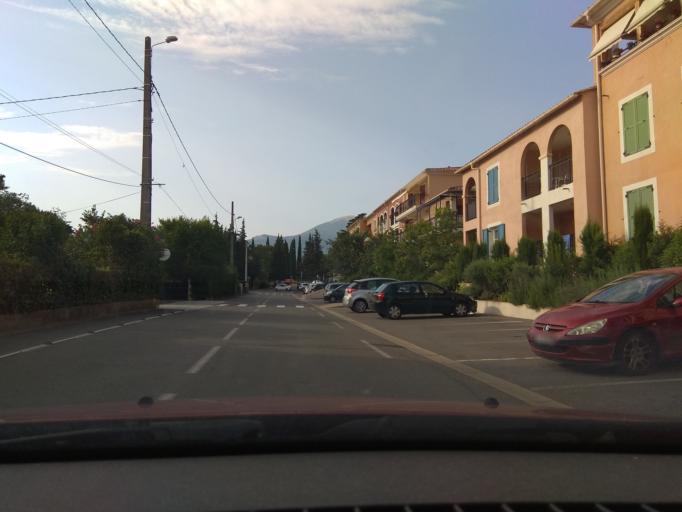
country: FR
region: Provence-Alpes-Cote d'Azur
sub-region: Departement des Alpes-Maritimes
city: Le Rouret
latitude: 43.6659
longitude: 7.0478
